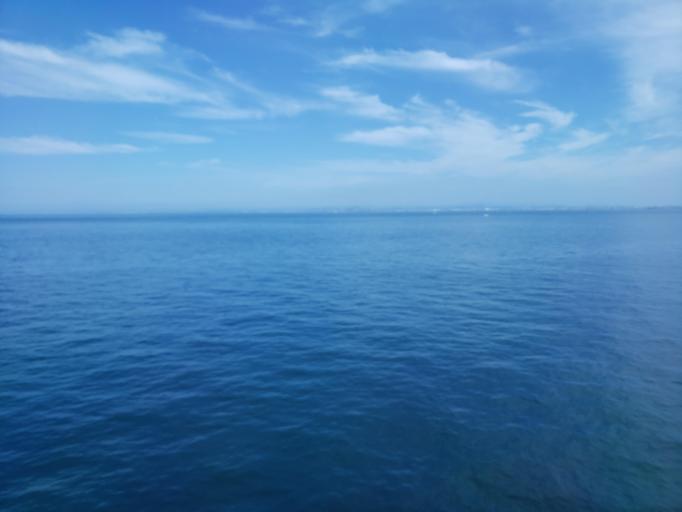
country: JP
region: Hyogo
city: Akashi
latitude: 34.5872
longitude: 134.8770
